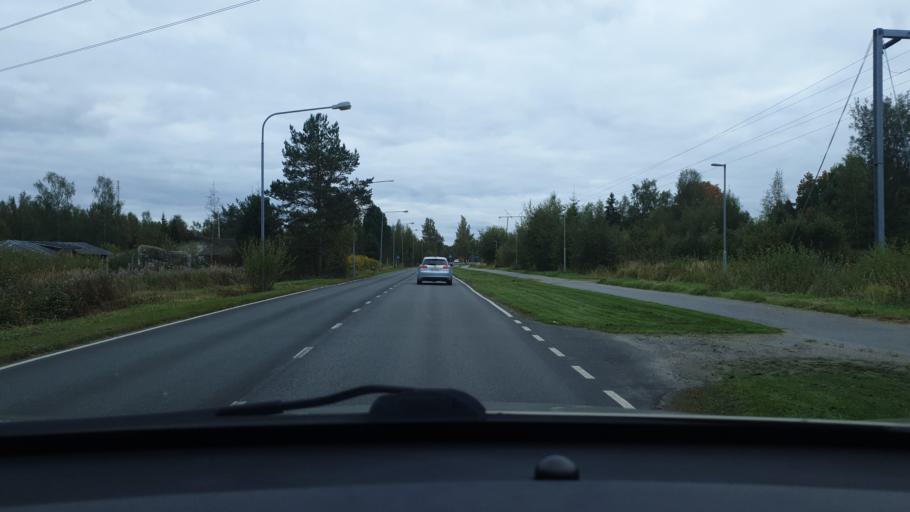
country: FI
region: Ostrobothnia
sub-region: Vaasa
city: Teeriniemi
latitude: 63.0925
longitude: 21.6983
